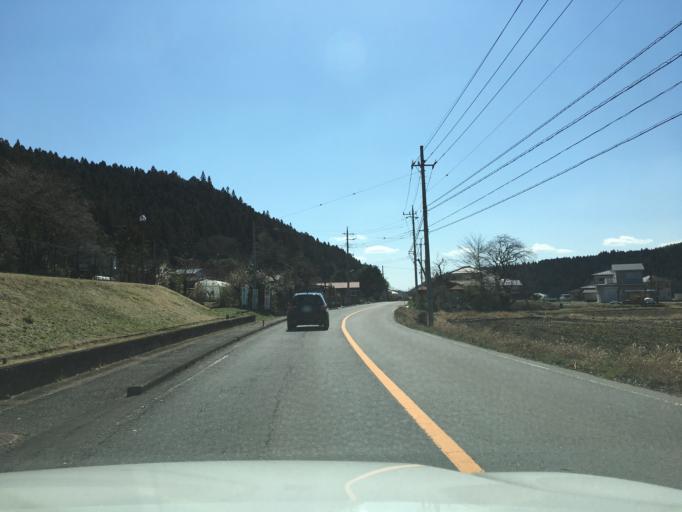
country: JP
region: Tochigi
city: Kuroiso
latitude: 36.9684
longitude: 140.1584
